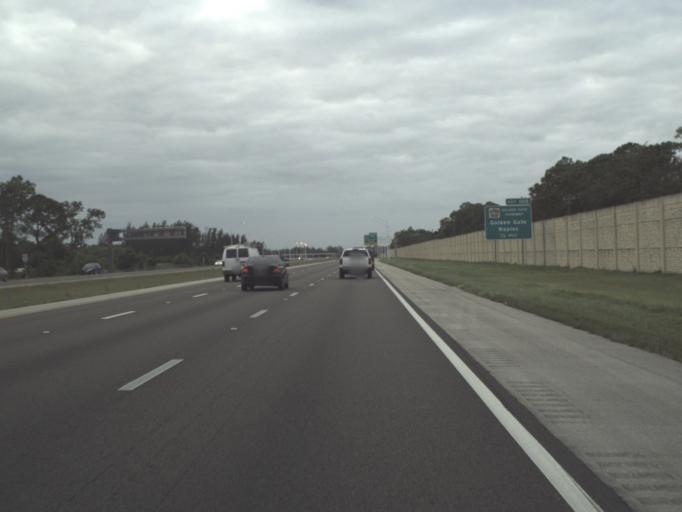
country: US
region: Florida
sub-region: Collier County
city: Golden Gate
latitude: 26.1891
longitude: -81.7359
